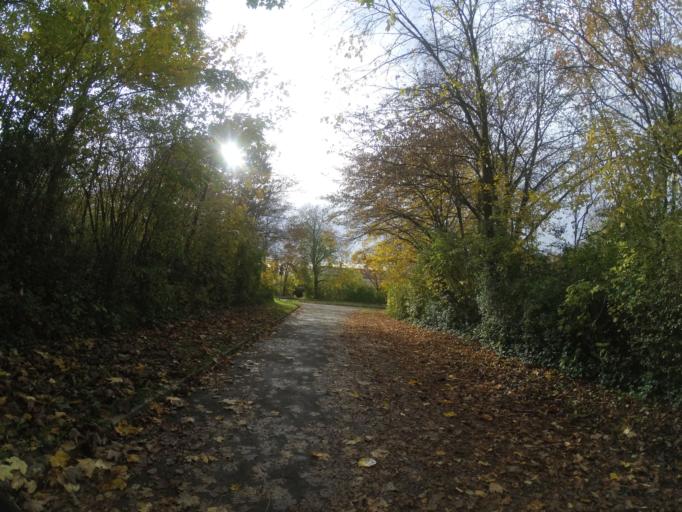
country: DE
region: Baden-Wuerttemberg
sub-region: Tuebingen Region
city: Ulm
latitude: 48.3609
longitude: 9.9798
